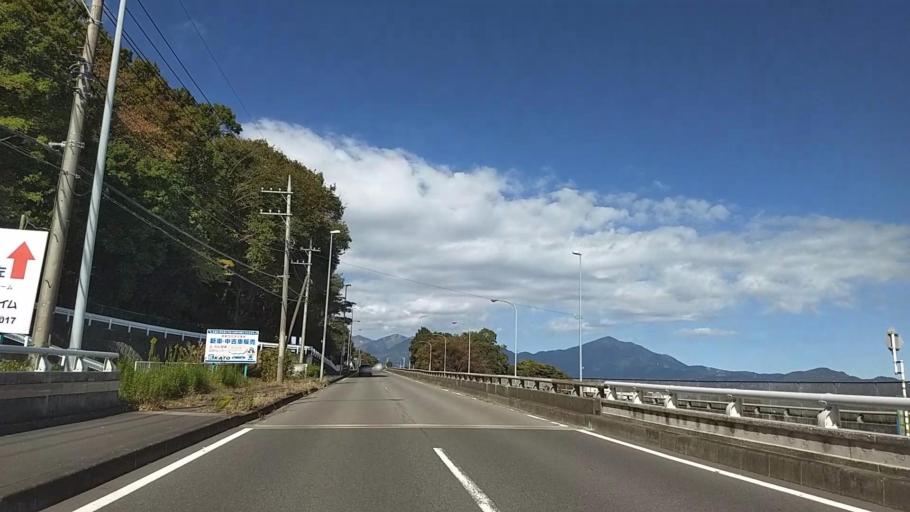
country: JP
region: Kanagawa
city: Ninomiya
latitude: 35.3318
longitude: 139.2314
